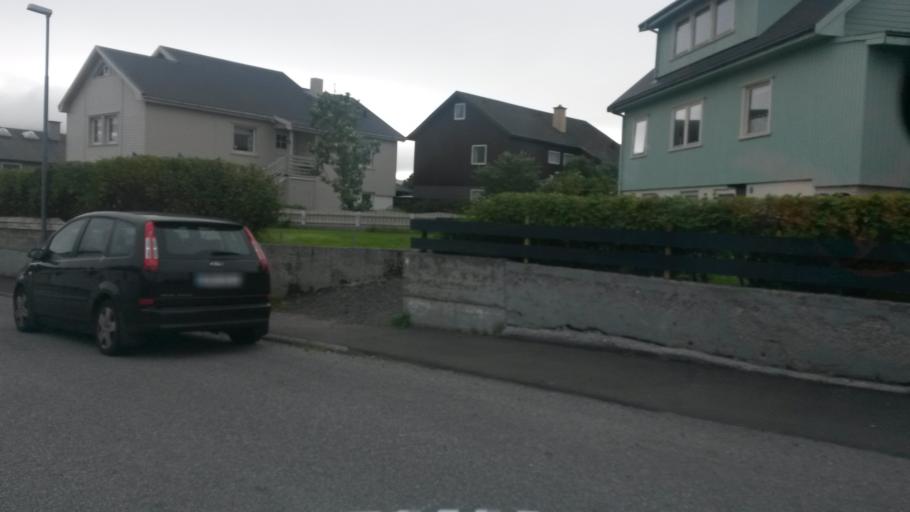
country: FO
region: Streymoy
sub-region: Torshavn
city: Torshavn
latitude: 62.0131
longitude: -6.7630
